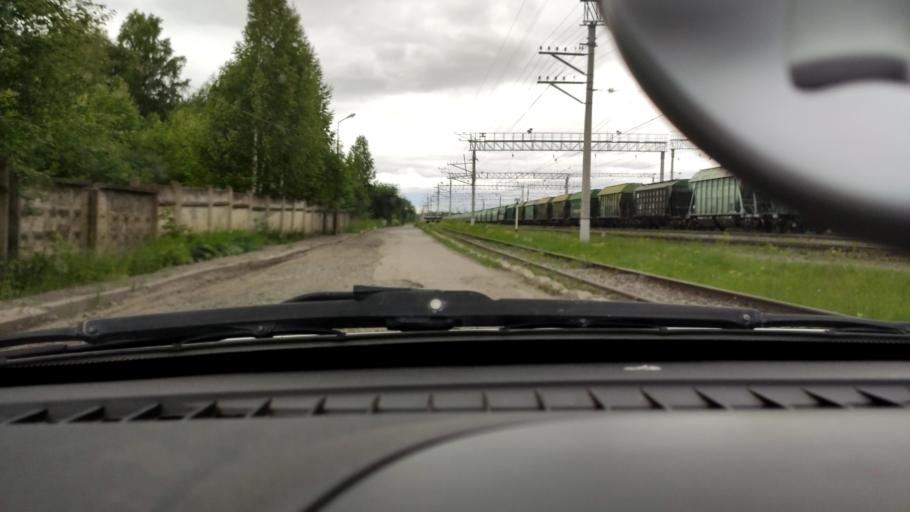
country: RU
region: Perm
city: Ferma
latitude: 57.8903
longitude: 56.2991
